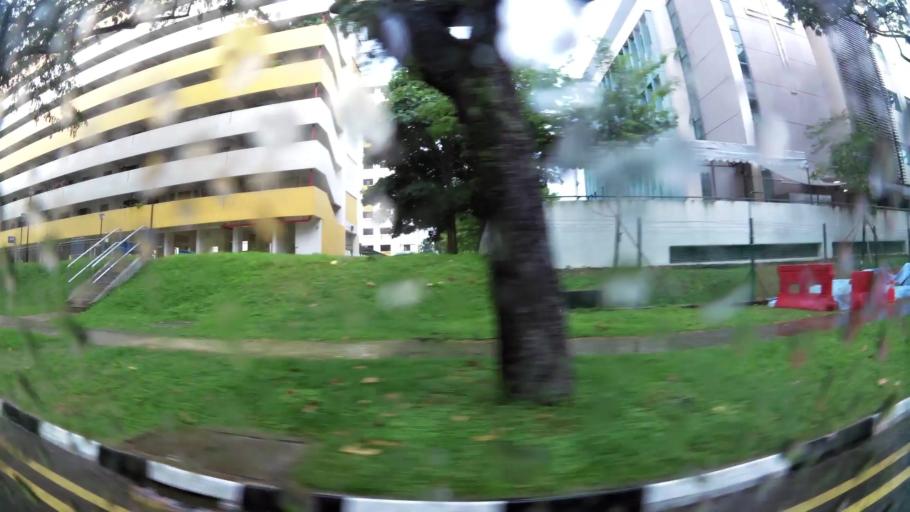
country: SG
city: Singapore
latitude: 1.3670
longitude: 103.8351
